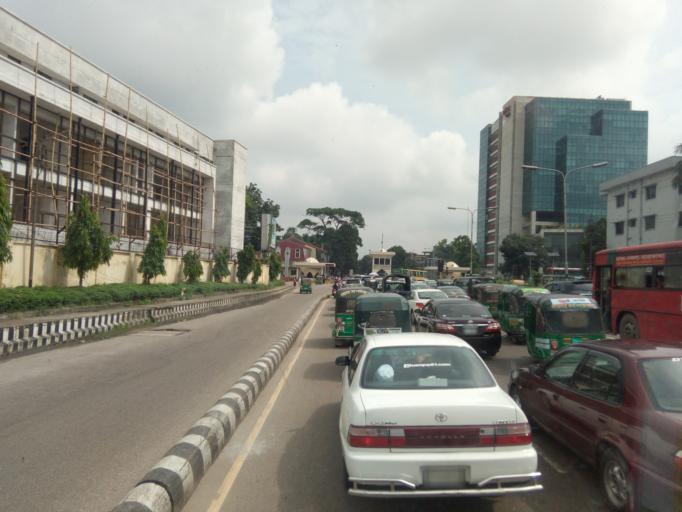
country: BD
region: Dhaka
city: Azimpur
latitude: 23.7745
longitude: 90.3899
